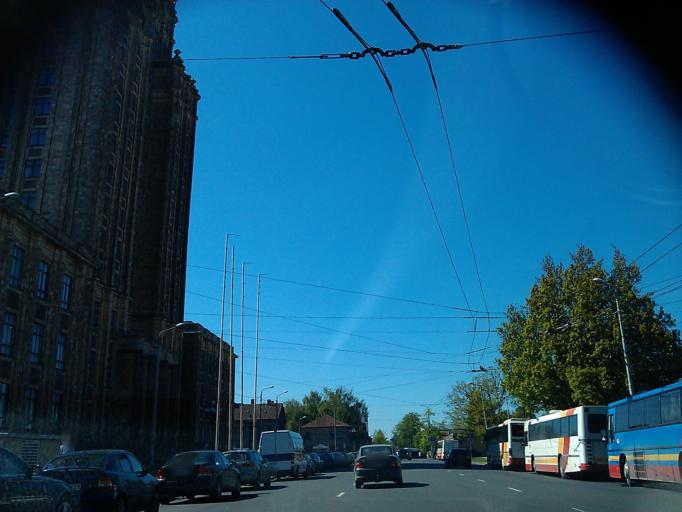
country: LV
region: Riga
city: Riga
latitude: 56.9442
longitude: 24.1224
